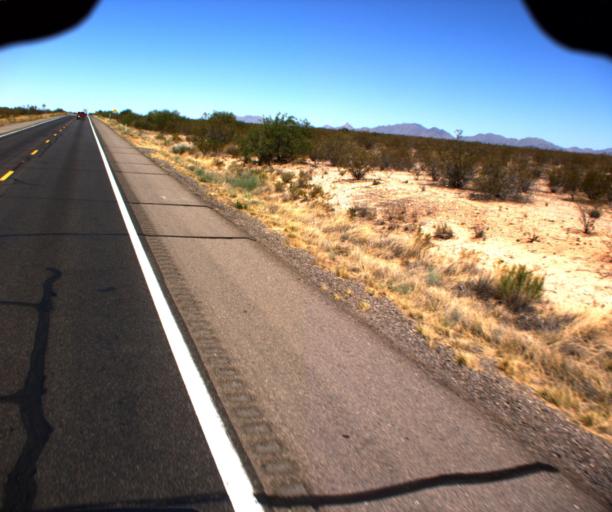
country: US
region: Arizona
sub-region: Yavapai County
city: Congress
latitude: 34.0469
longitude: -112.8406
